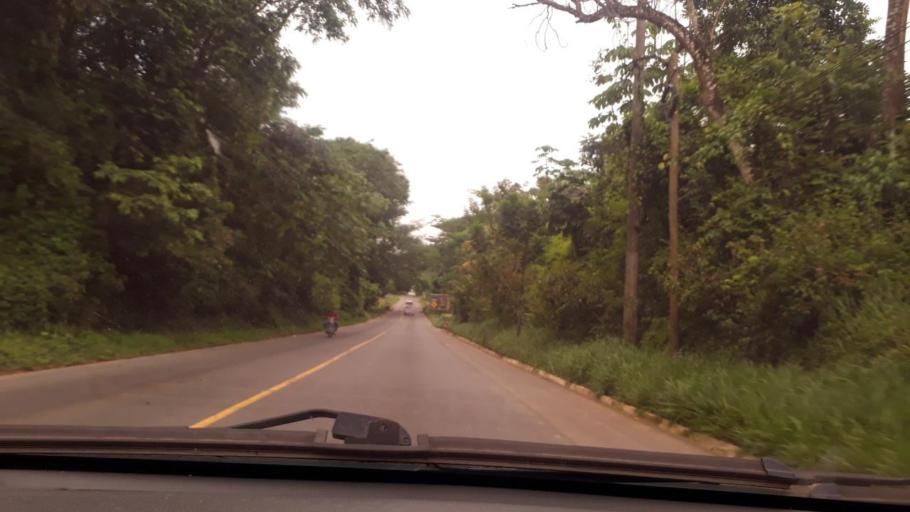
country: GT
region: Izabal
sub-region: Municipio de Puerto Barrios
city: Puerto Barrios
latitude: 15.6205
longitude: -88.5638
